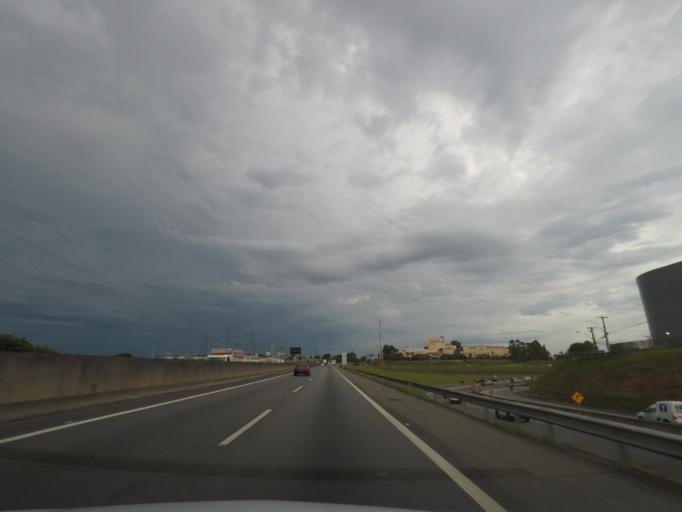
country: BR
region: Sao Paulo
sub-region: Campinas
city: Campinas
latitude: -22.9314
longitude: -47.0763
